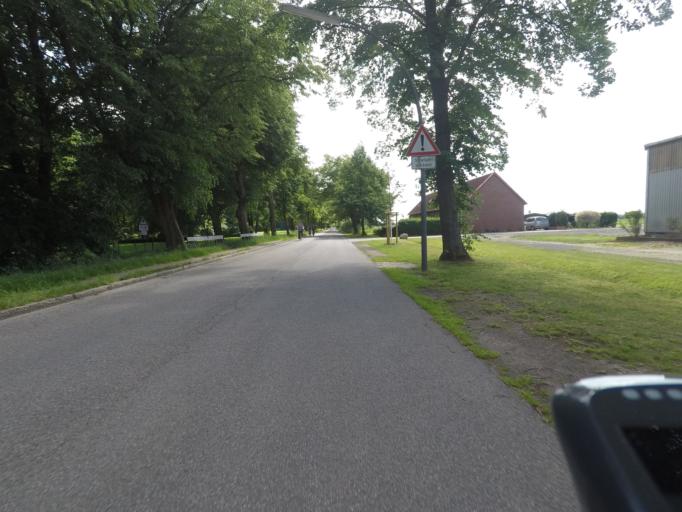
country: DE
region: Lower Saxony
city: Drage
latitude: 53.4370
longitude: 10.2331
